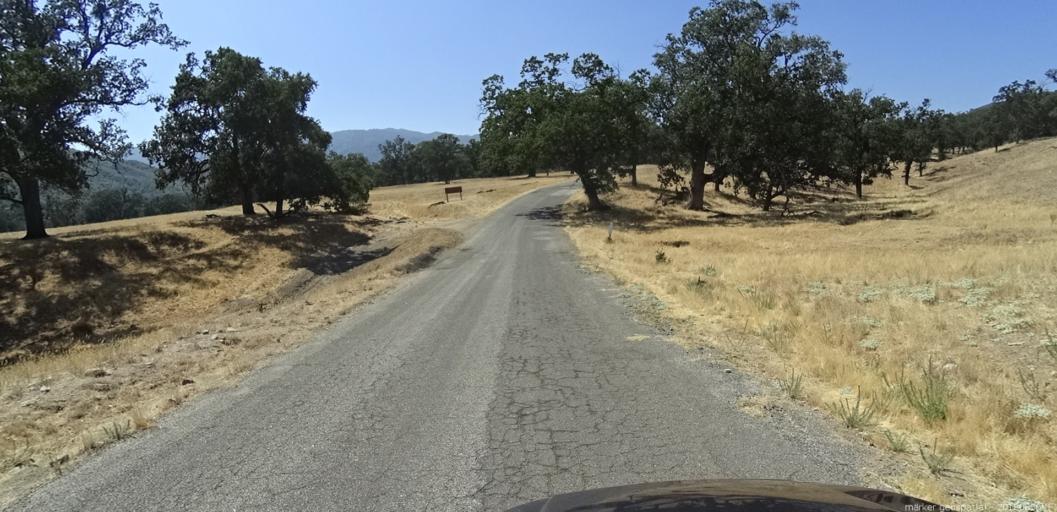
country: US
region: California
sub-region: Monterey County
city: Greenfield
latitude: 36.0884
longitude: -121.4107
